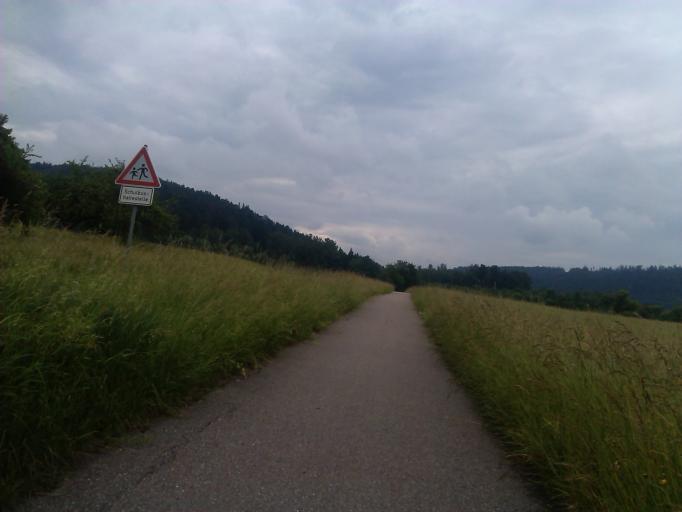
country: DE
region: Baden-Wuerttemberg
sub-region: Regierungsbezirk Stuttgart
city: Oberrot
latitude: 48.9993
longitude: 9.6852
